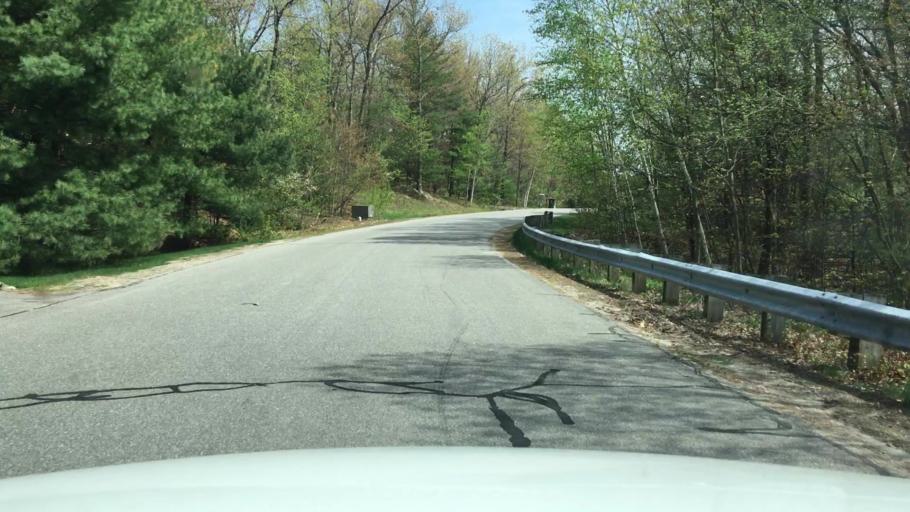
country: US
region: New Hampshire
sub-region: Rockingham County
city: Londonderry
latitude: 42.8291
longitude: -71.3739
